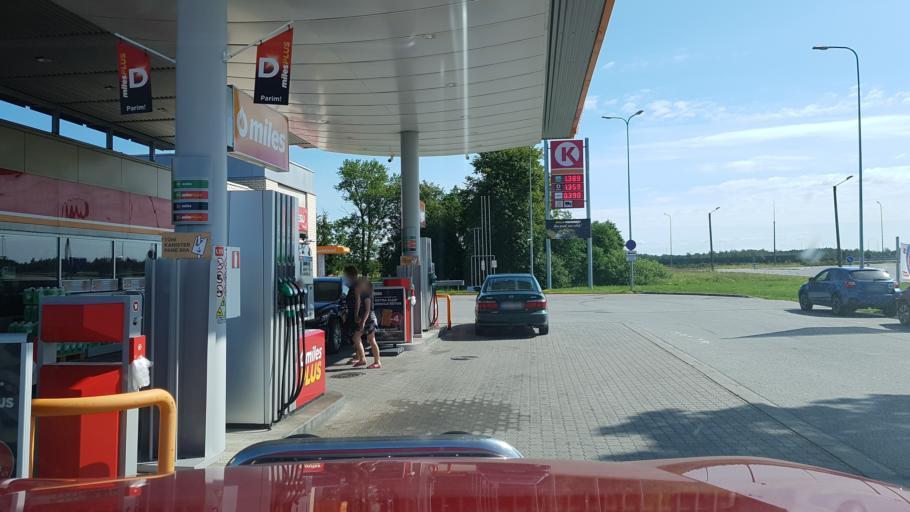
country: EE
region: Jaervamaa
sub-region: Paide linn
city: Paide
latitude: 58.9183
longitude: 25.6106
